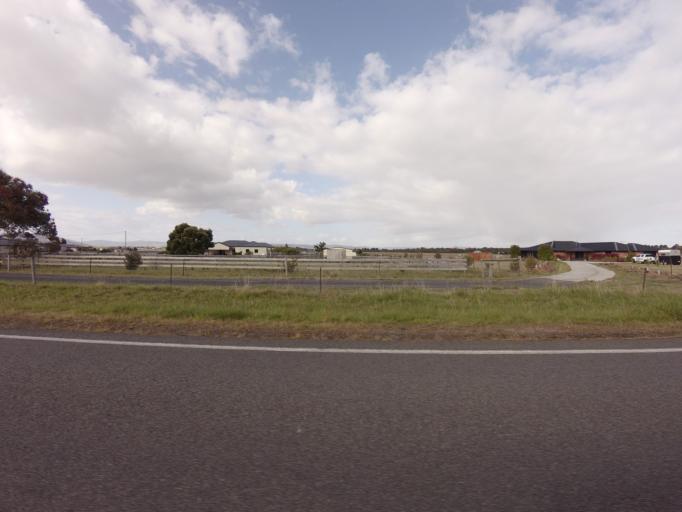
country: AU
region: Tasmania
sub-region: Clarence
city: Seven Mile Beach
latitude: -42.8498
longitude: 147.4837
